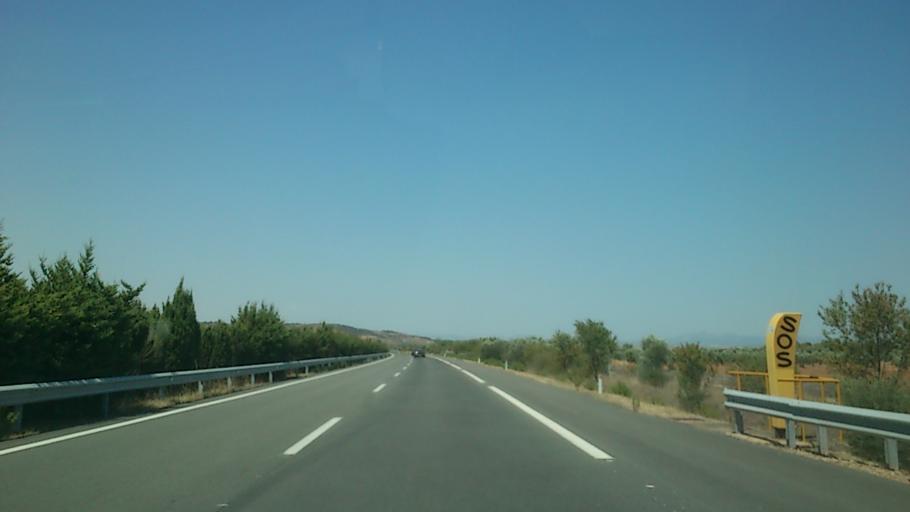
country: ES
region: La Rioja
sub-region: Provincia de La Rioja
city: Pradejon
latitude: 42.3351
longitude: -2.0175
